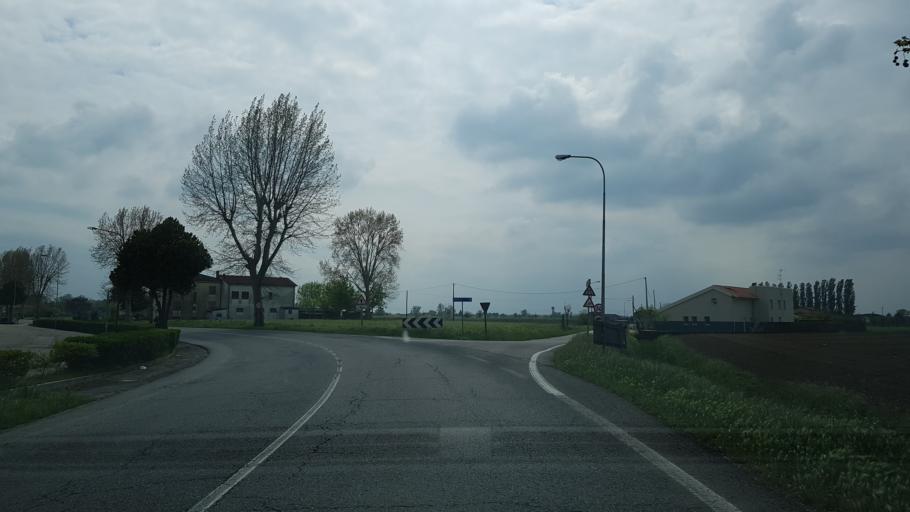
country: IT
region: Veneto
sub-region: Provincia di Verona
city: Minerbe
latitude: 45.2345
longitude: 11.3309
